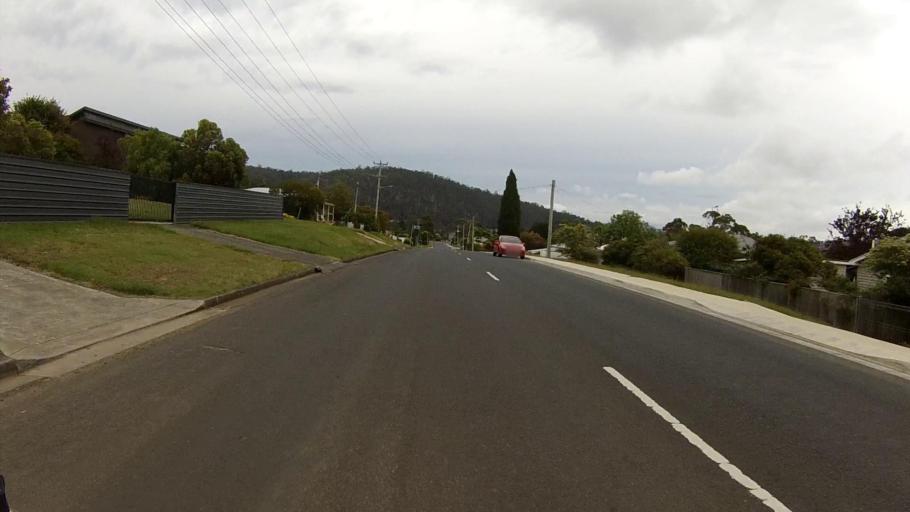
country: AU
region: Tasmania
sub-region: Sorell
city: Sorell
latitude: -42.5651
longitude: 147.8734
